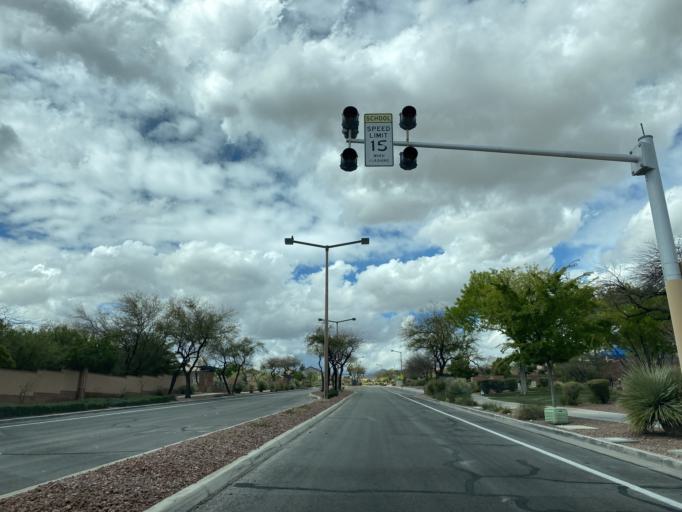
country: US
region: Nevada
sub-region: Clark County
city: Summerlin South
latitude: 36.1899
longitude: -115.3330
